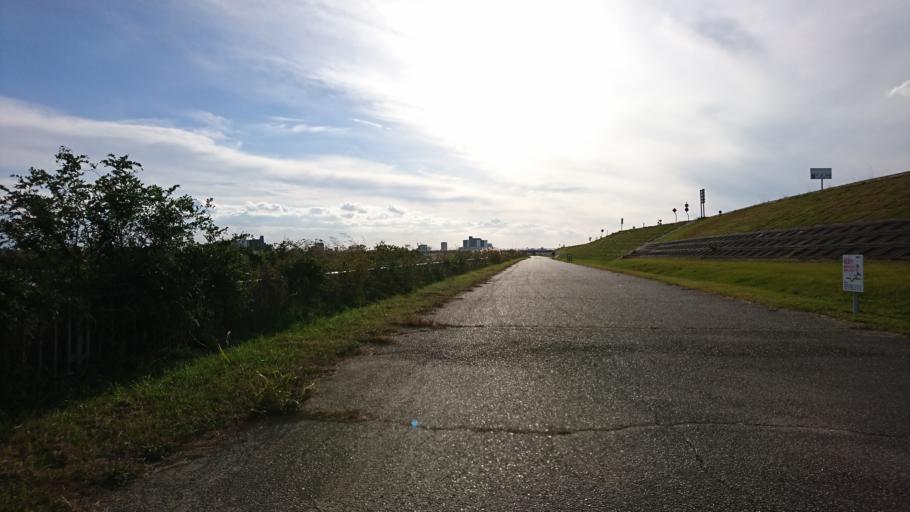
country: JP
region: Hyogo
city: Kakogawacho-honmachi
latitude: 34.7824
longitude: 134.8451
